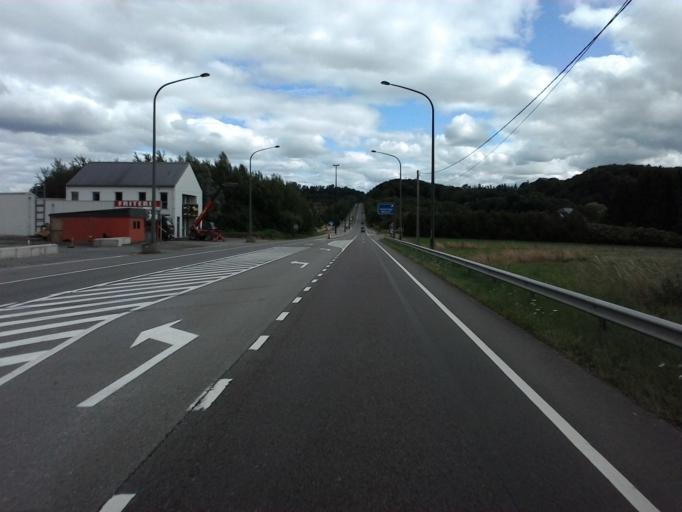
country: BE
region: Wallonia
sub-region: Province du Luxembourg
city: Attert
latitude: 49.7256
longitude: 5.7965
